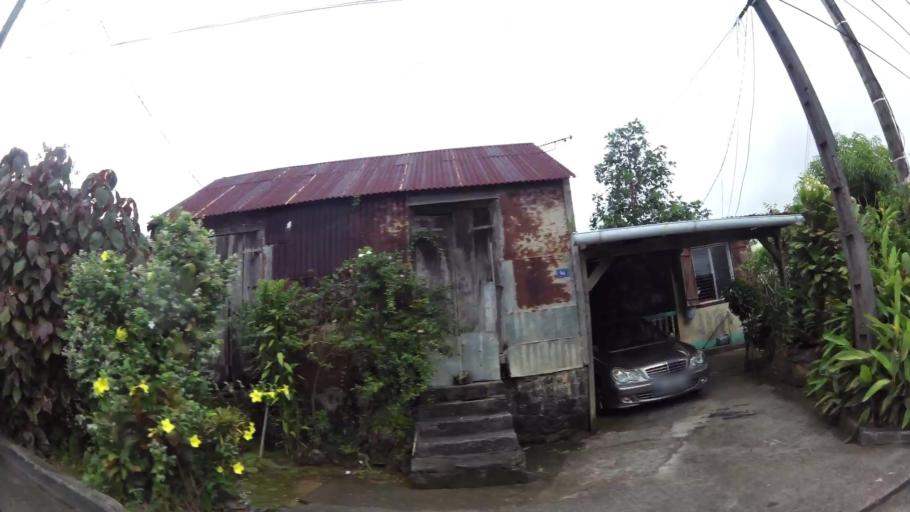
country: GP
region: Guadeloupe
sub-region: Guadeloupe
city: Trois-Rivieres
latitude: 15.9916
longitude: -61.6547
